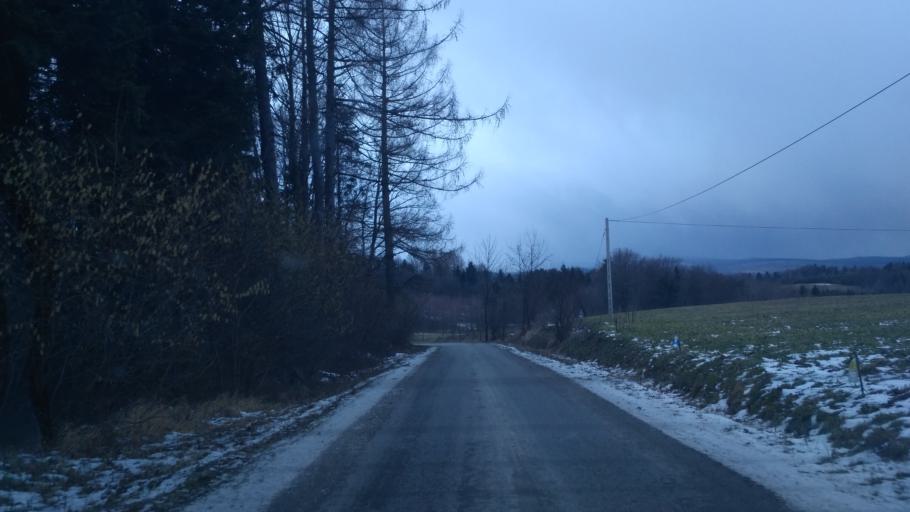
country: PL
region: Subcarpathian Voivodeship
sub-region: Powiat rzeszowski
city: Hyzne
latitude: 49.8930
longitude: 22.1487
